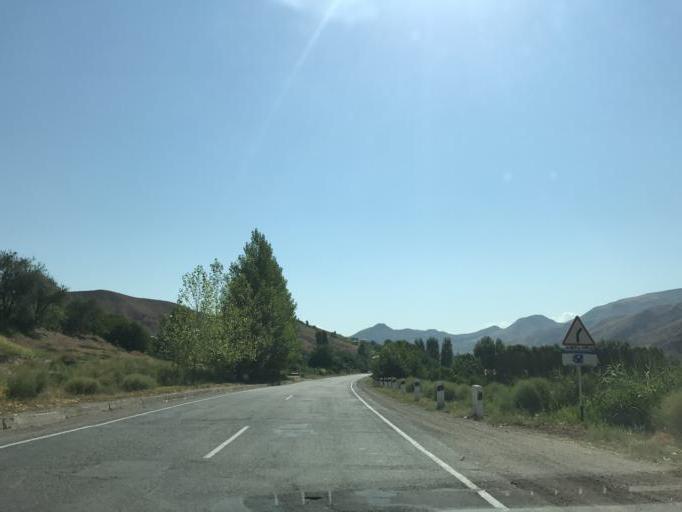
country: AM
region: Vayots' Dzori Marz
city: Getap'
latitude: 39.7387
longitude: 45.2616
